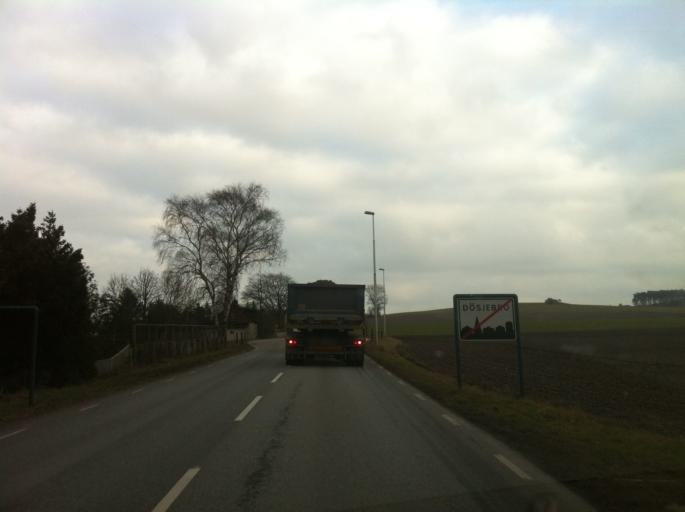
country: SE
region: Skane
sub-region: Kavlinge Kommun
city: Loddekopinge
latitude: 55.8192
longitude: 13.0293
